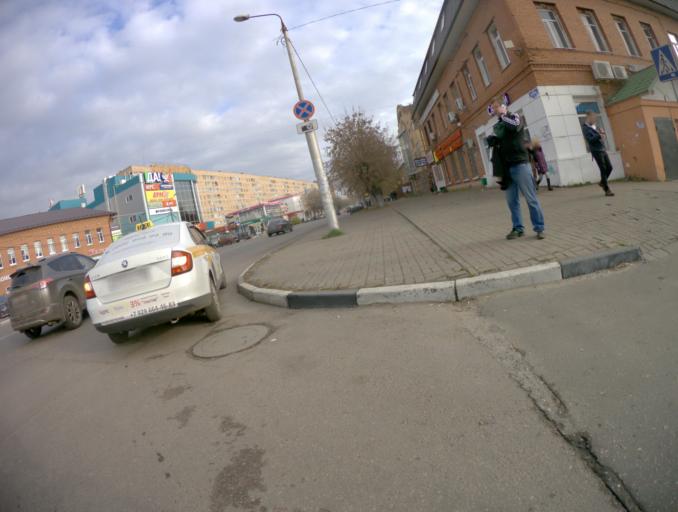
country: RU
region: Moskovskaya
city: Orekhovo-Zuyevo
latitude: 55.7968
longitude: 38.9747
